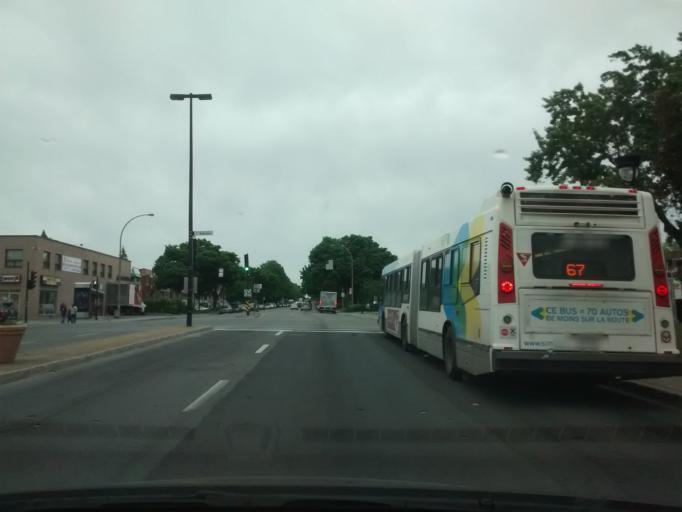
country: CA
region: Quebec
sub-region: Montreal
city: Saint-Leonard
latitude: 45.5575
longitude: -73.5945
